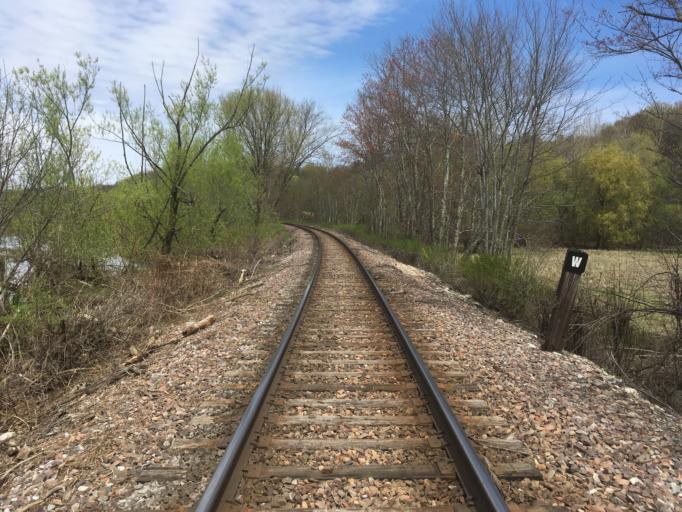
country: US
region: Vermont
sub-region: Rutland County
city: Brandon
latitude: 43.7081
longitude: -73.0363
